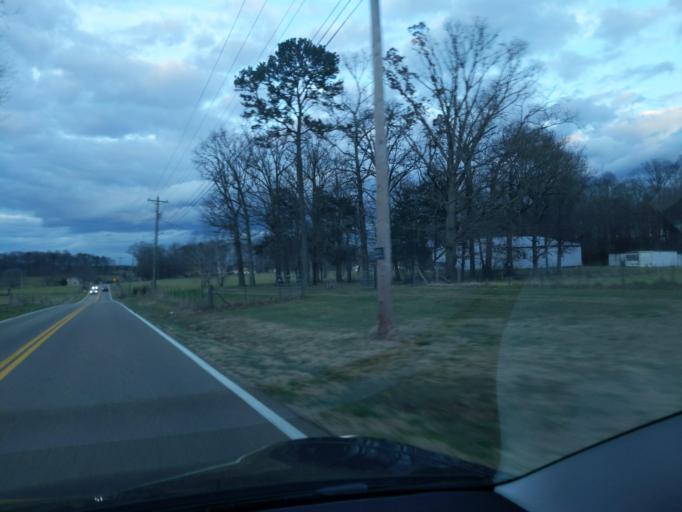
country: US
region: Tennessee
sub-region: Jefferson County
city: White Pine
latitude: 36.0946
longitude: -83.3586
